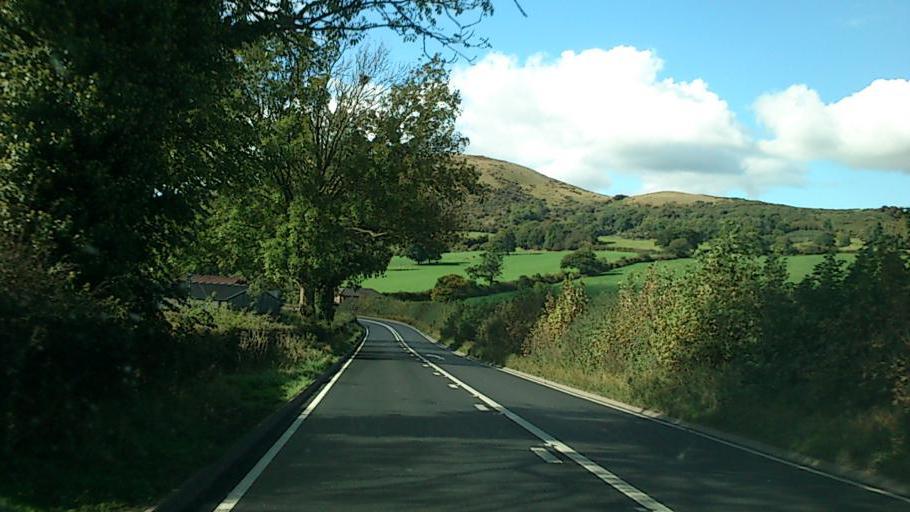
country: GB
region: England
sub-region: Shropshire
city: Westbury
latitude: 52.7067
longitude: -3.0115
